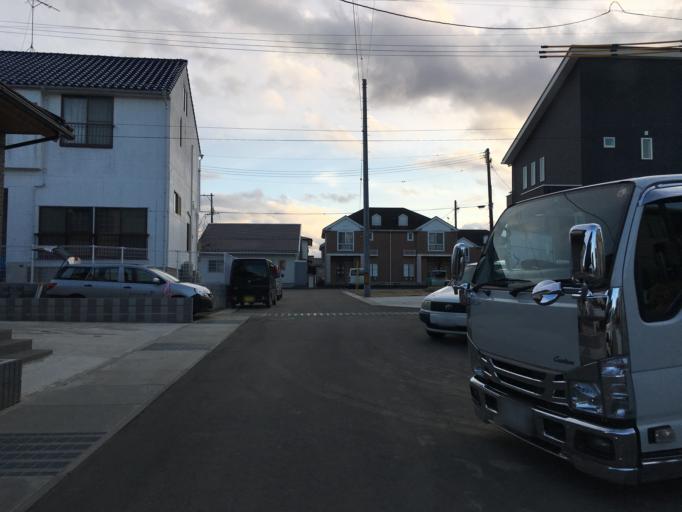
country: JP
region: Fukushima
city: Hobaramachi
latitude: 37.8084
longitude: 140.4888
